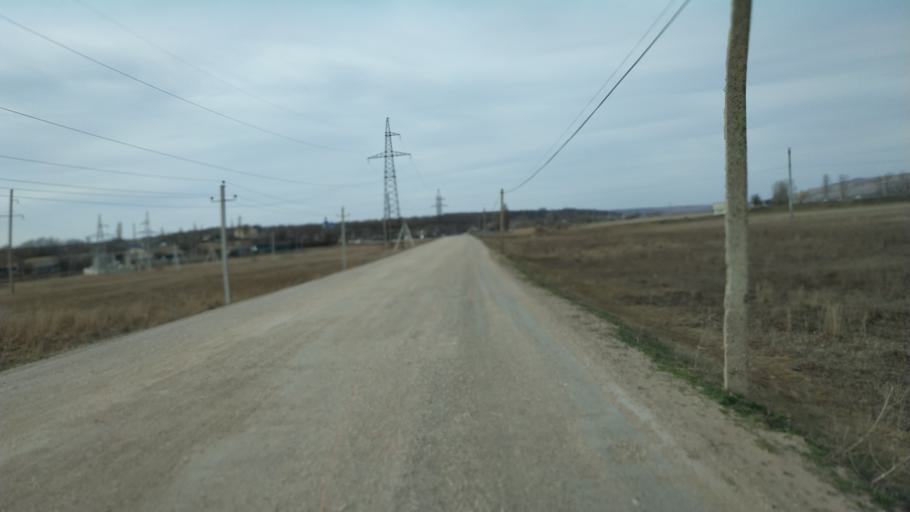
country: RO
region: Vaslui
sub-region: Comuna Dranceni
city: Dranceni
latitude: 46.8575
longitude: 28.2055
